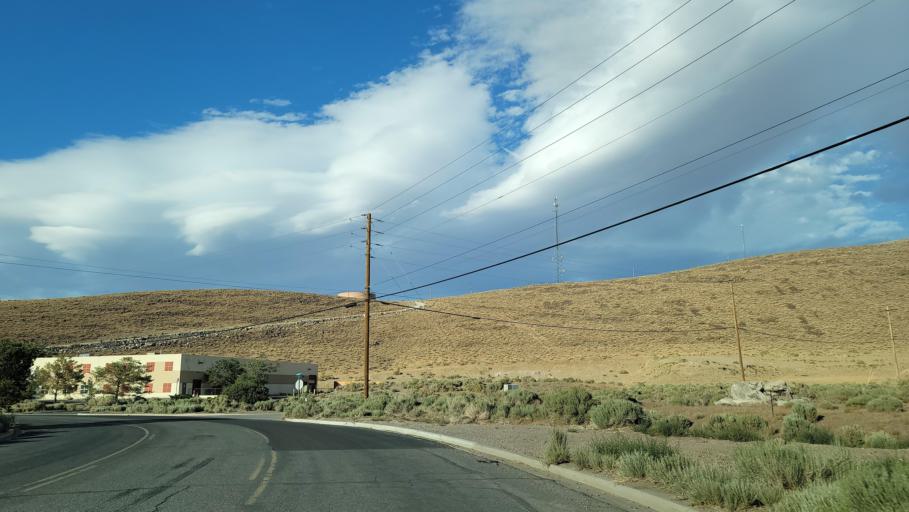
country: US
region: Nevada
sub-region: Washoe County
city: Spanish Springs
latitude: 39.5510
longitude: -119.5404
